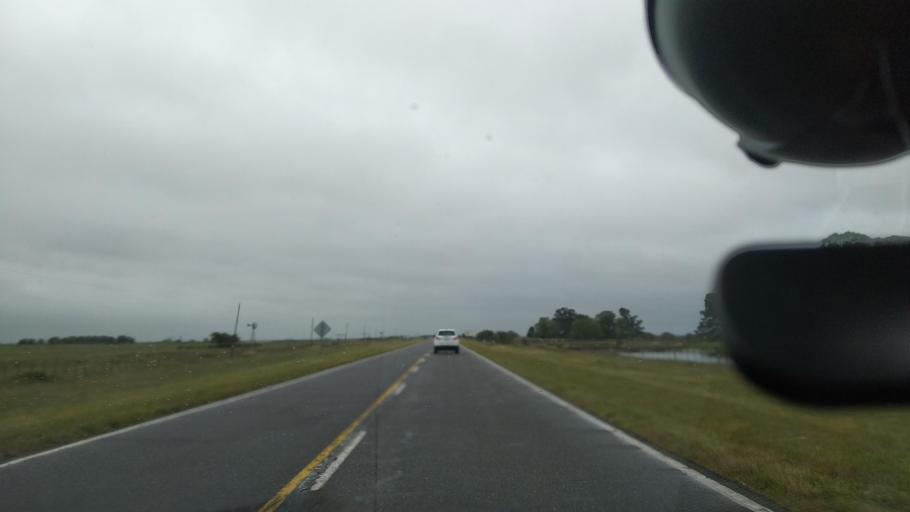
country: AR
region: Buenos Aires
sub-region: Partido de Dolores
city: Dolores
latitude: -36.1020
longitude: -57.4332
